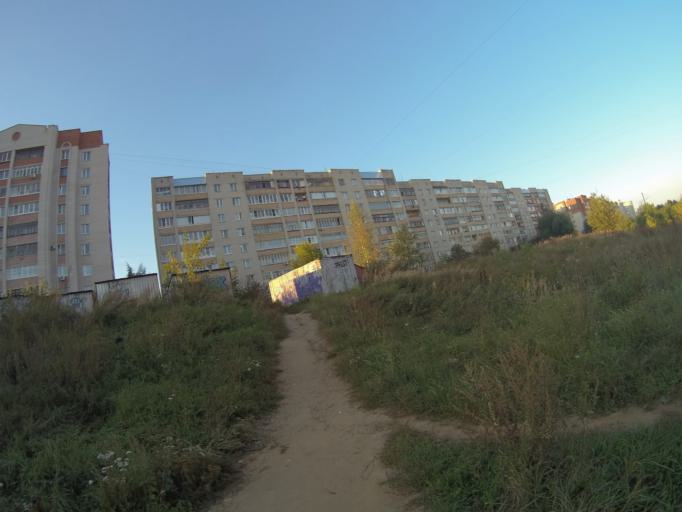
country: RU
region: Vladimir
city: Vladimir
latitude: 56.1100
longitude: 40.3514
